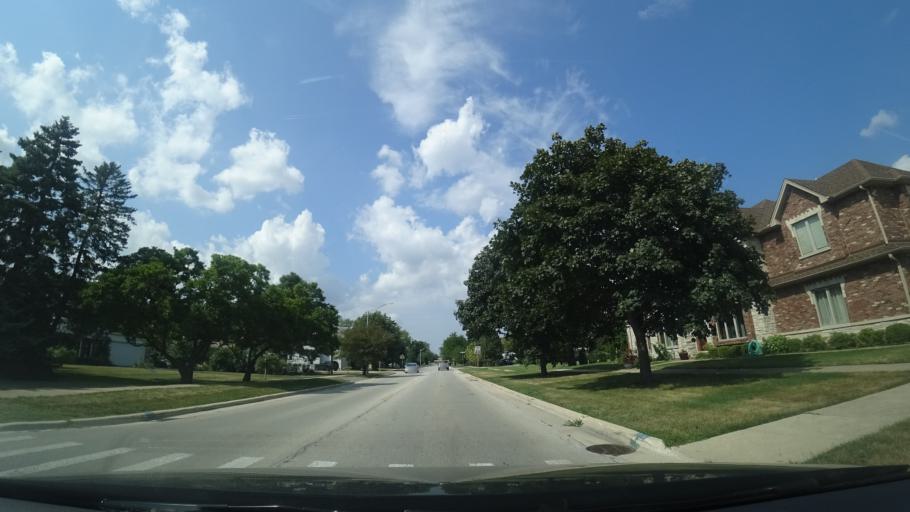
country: US
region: Illinois
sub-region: Cook County
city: Norridge
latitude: 41.9700
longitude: -87.8267
